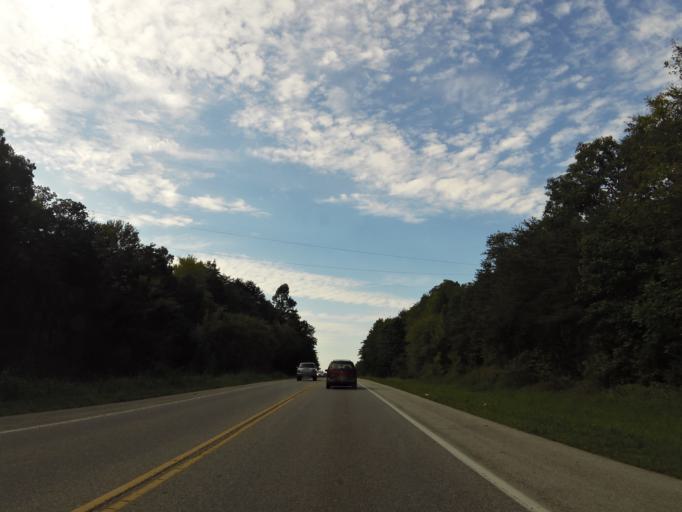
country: US
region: Tennessee
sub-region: Monroe County
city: Vonore
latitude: 35.5951
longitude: -84.2735
